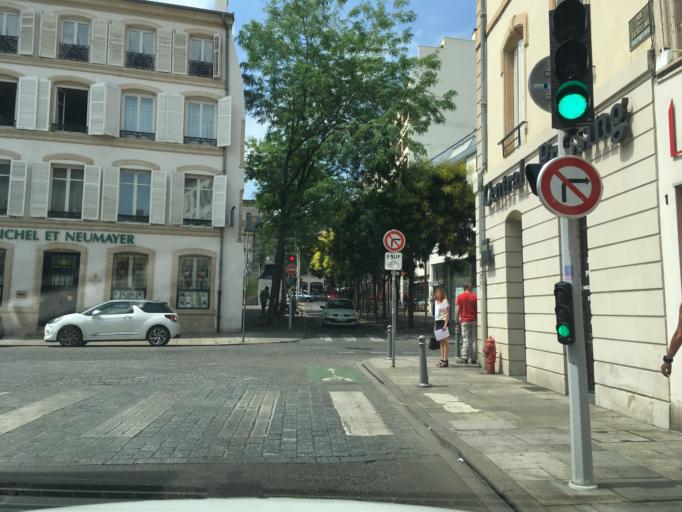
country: FR
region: Lorraine
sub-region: Departement de Meurthe-et-Moselle
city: Nancy
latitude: 48.6896
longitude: 6.1852
